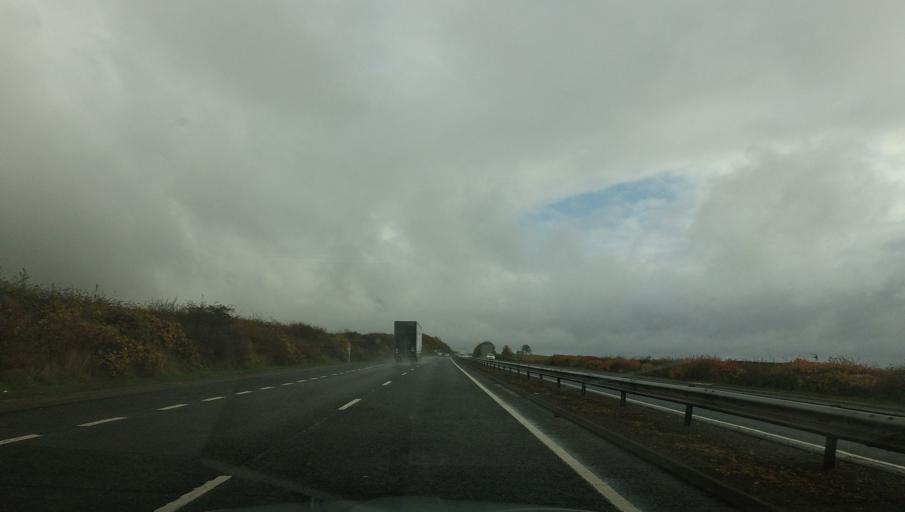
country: GB
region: Scotland
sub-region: Fife
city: Lochgelly
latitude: 56.1158
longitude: -3.3129
